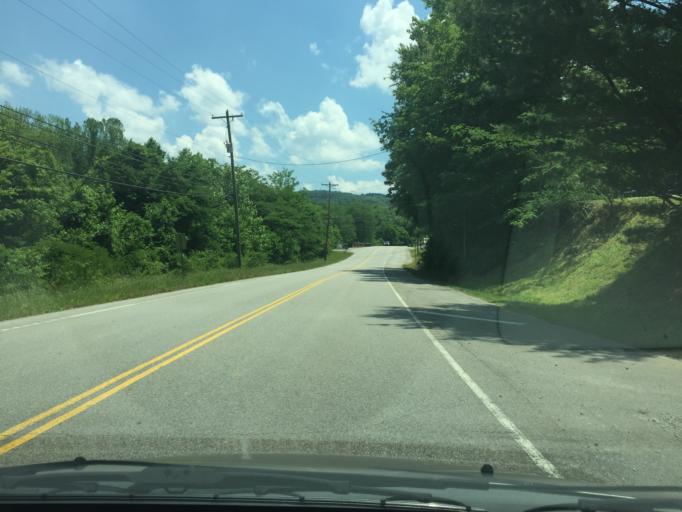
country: US
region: Tennessee
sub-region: Hamilton County
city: Lookout Mountain
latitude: 35.0364
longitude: -85.4144
